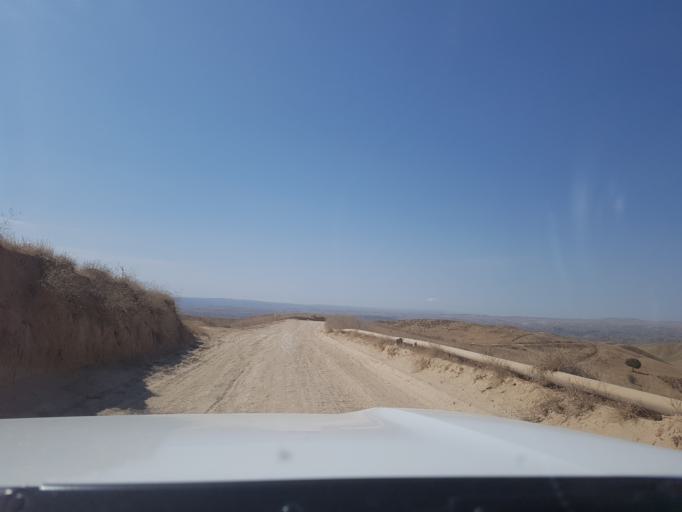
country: TM
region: Ahal
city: Baharly
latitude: 38.2684
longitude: 56.8924
